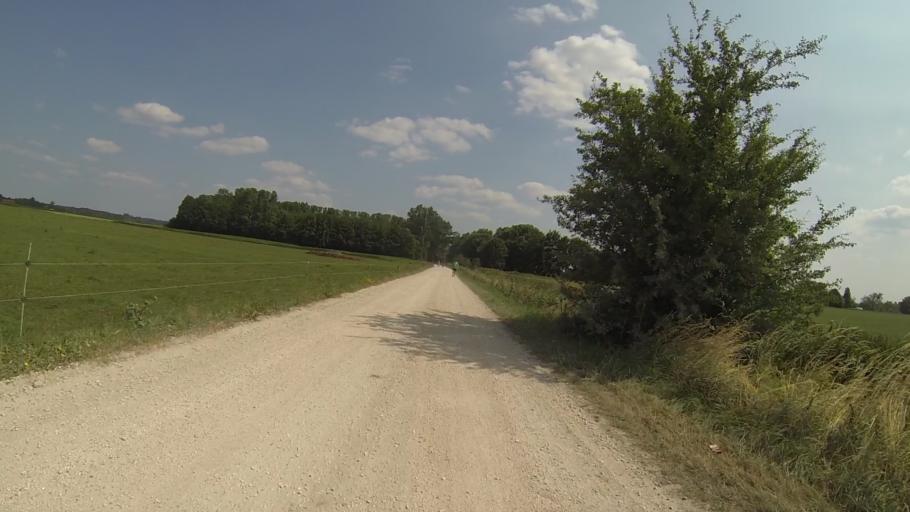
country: DE
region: Bavaria
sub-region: Swabia
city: Guenzburg
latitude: 48.4974
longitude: 10.2691
